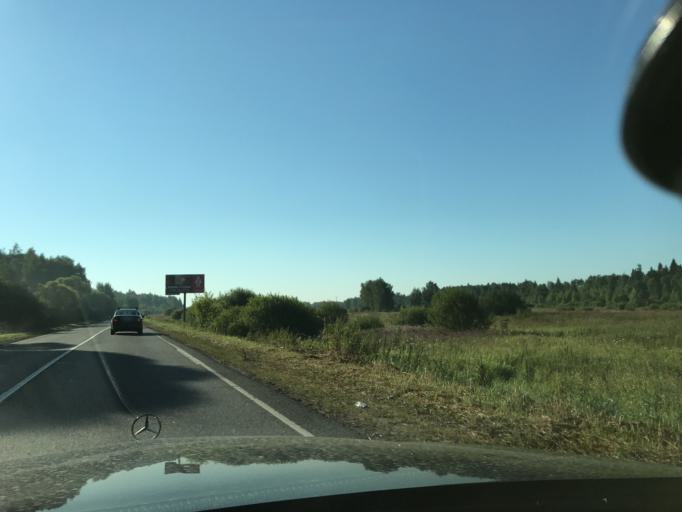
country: RU
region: Moskovskaya
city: Bakhchivandzhi
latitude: 55.8571
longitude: 38.0667
